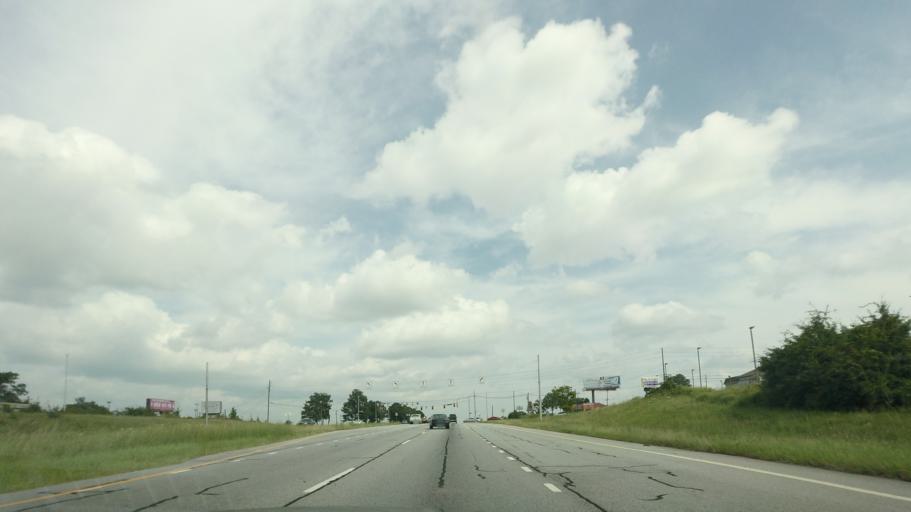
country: US
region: Georgia
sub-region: Bibb County
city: Macon
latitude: 32.8159
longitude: -83.7000
